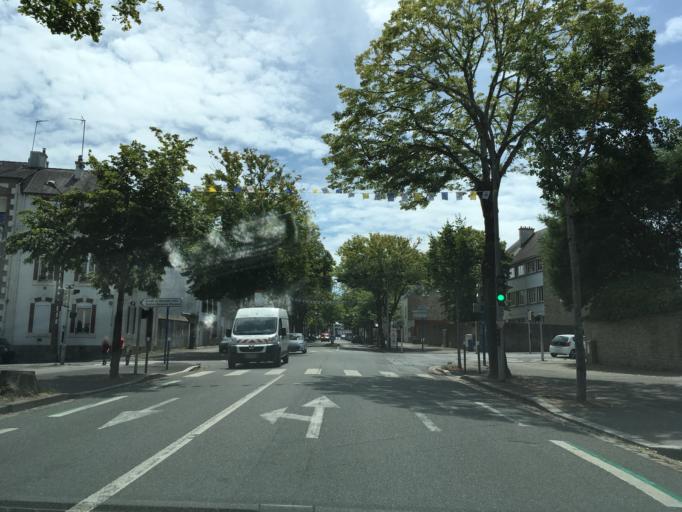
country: FR
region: Brittany
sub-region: Departement du Morbihan
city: Lorient
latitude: 47.7431
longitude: -3.3683
